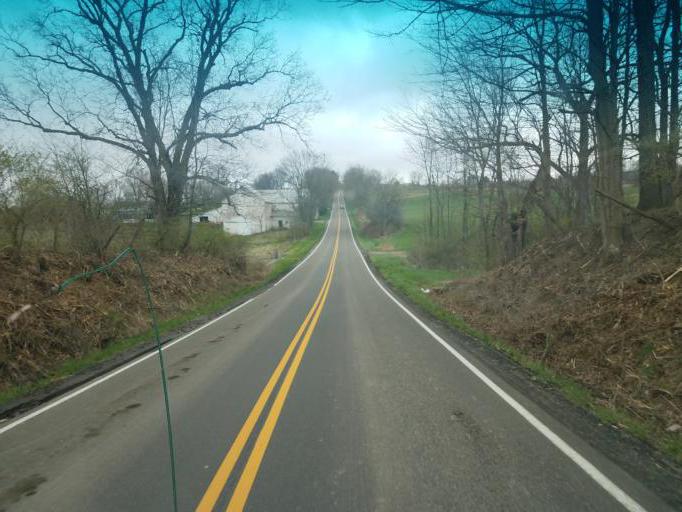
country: US
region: Ohio
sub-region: Stark County
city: Beach City
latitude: 40.6176
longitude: -81.7069
